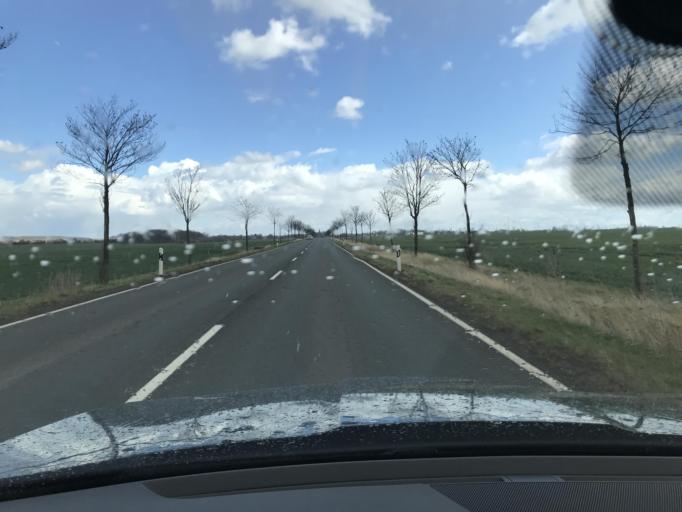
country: DE
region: Saxony-Anhalt
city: Hoym
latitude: 51.7844
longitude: 11.2834
